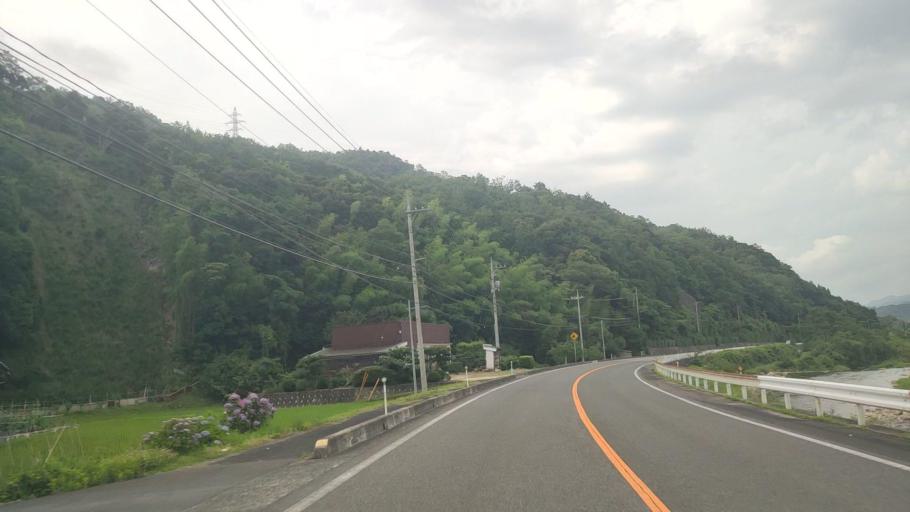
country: JP
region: Tottori
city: Kurayoshi
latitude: 35.3764
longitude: 133.8490
